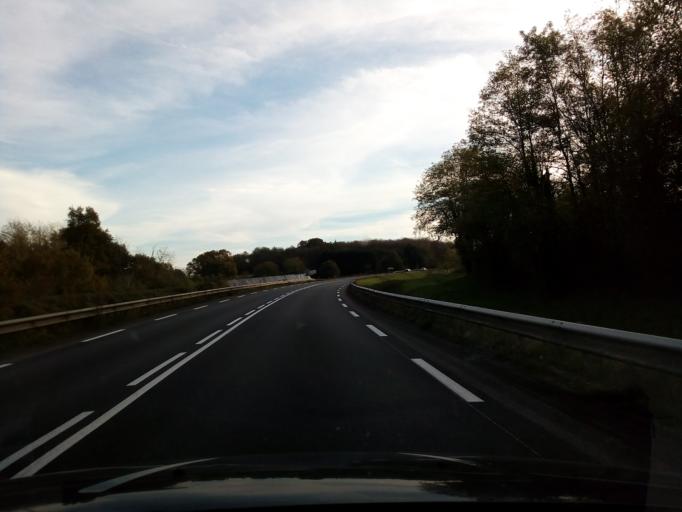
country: FR
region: Poitou-Charentes
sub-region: Departement de la Charente
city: Saint-Claud
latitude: 45.8624
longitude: 0.4670
